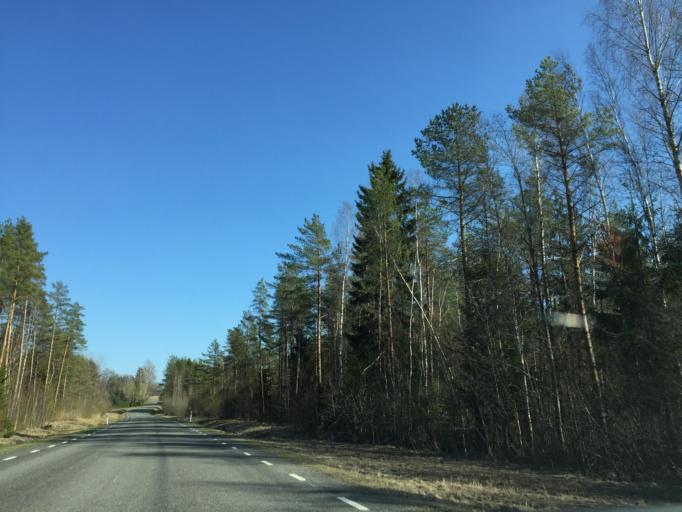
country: EE
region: Viljandimaa
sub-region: Viiratsi vald
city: Viiratsi
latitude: 58.2694
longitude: 25.6480
